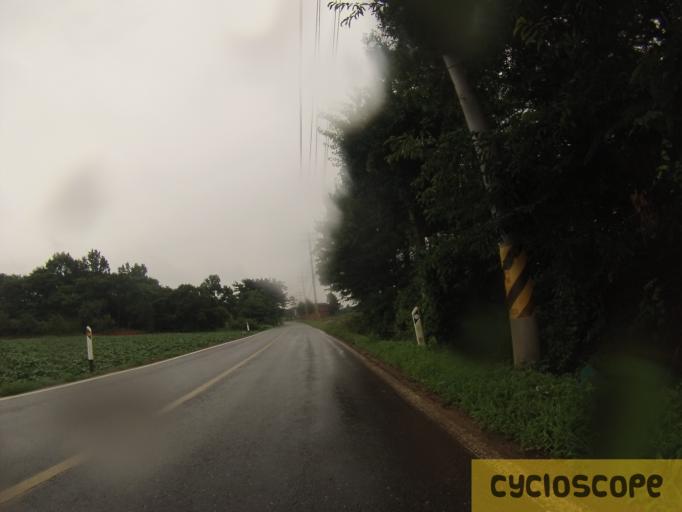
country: KR
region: Chungcheongnam-do
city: Taisen-ri
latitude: 36.1790
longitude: 126.5261
